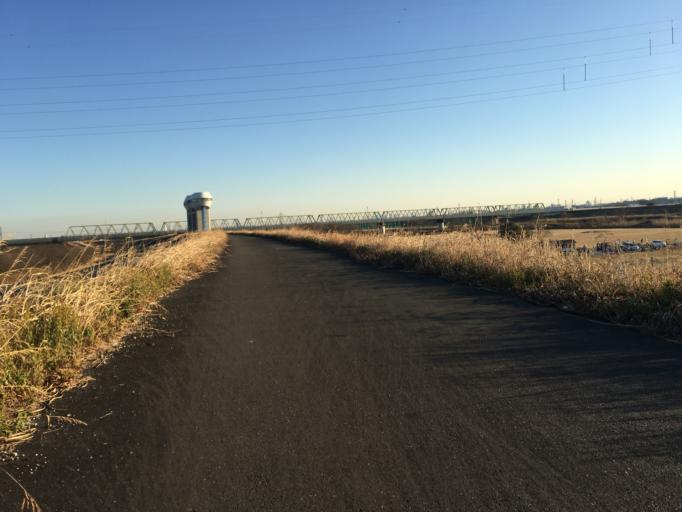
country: JP
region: Saitama
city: Shiki
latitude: 35.8357
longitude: 139.6104
